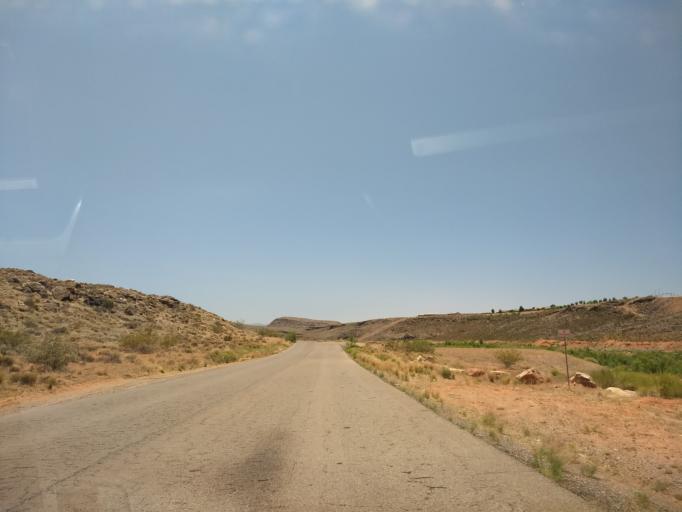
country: US
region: Utah
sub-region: Washington County
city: Washington
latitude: 37.1393
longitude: -113.4608
